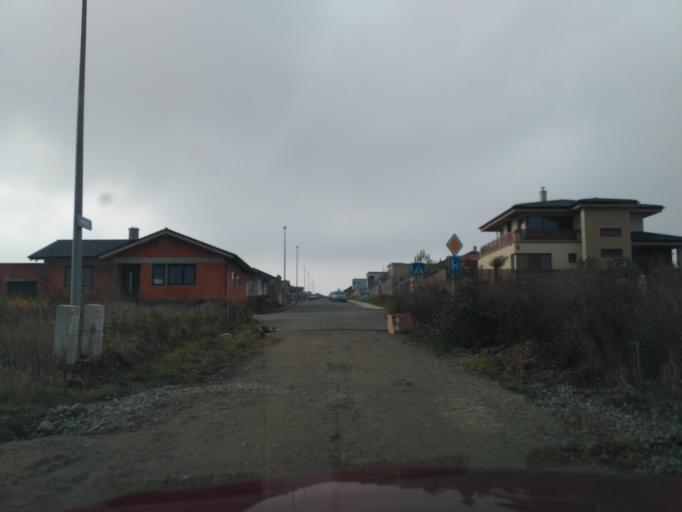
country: SK
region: Kosicky
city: Kosice
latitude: 48.6821
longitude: 21.3128
